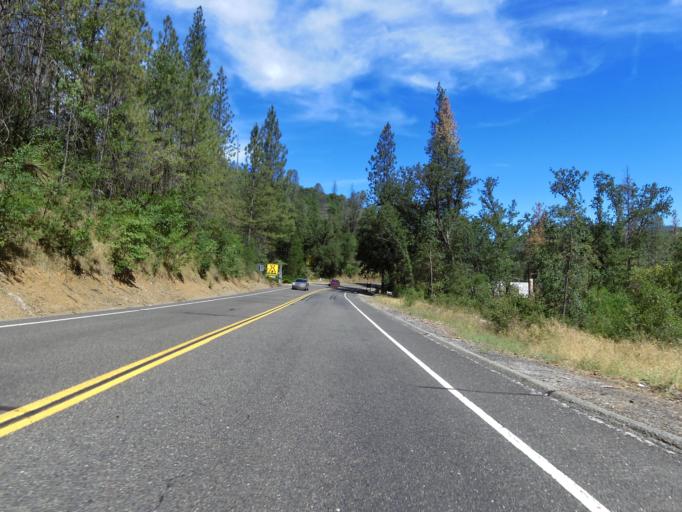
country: US
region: California
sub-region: Mariposa County
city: Midpines
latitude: 37.5432
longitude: -119.9193
